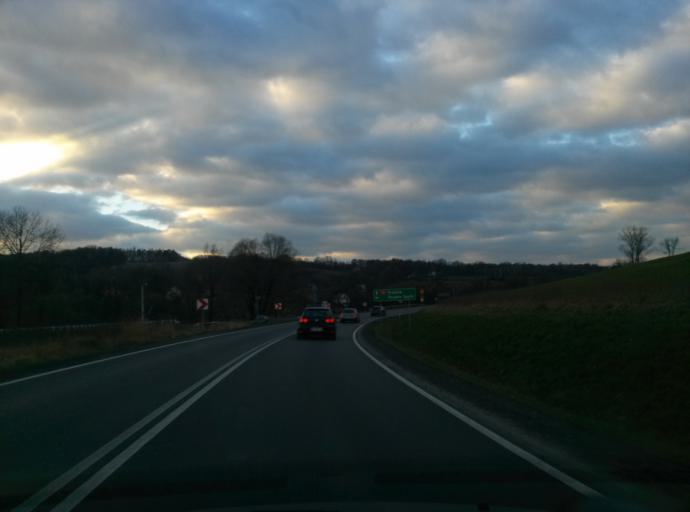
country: PL
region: Lesser Poland Voivodeship
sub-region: Powiat brzeski
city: Okocim
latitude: 49.9453
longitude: 20.5877
